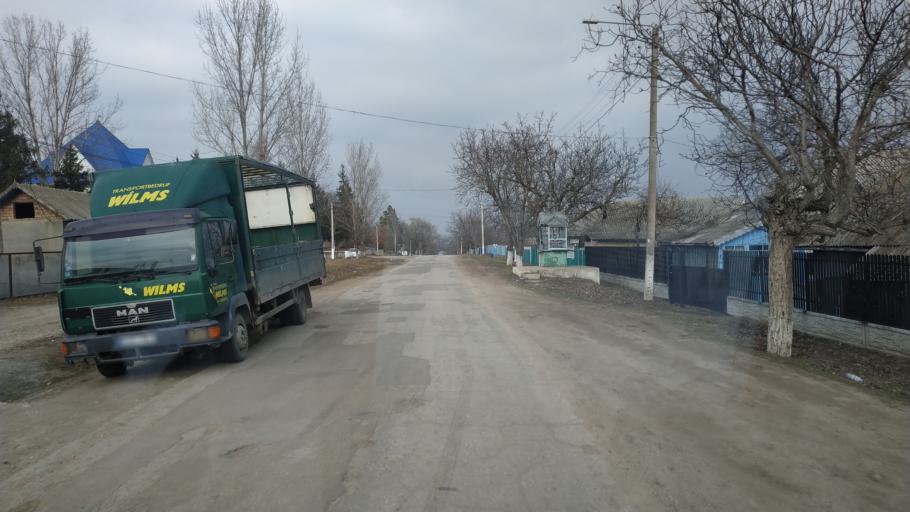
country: MD
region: Hincesti
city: Dancu
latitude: 46.8202
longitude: 28.2742
